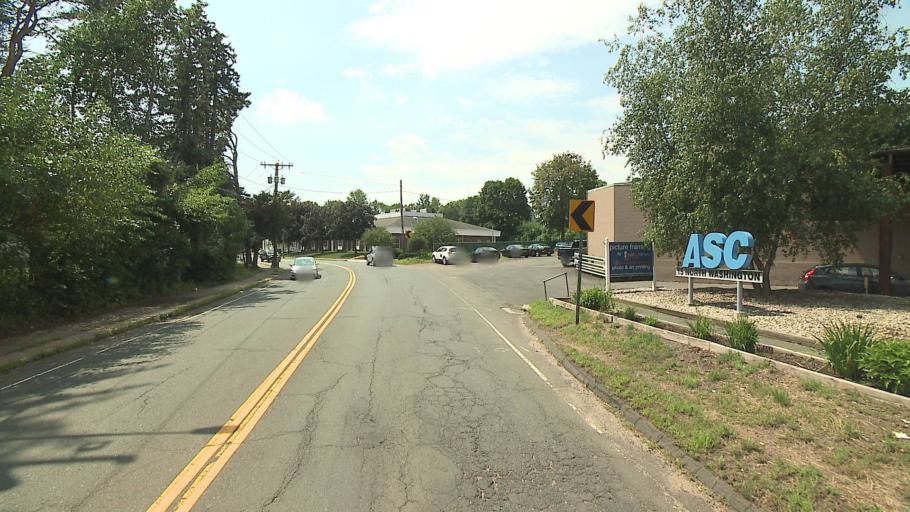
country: US
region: Connecticut
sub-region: Hartford County
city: Plainville
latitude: 41.6711
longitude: -72.8756
